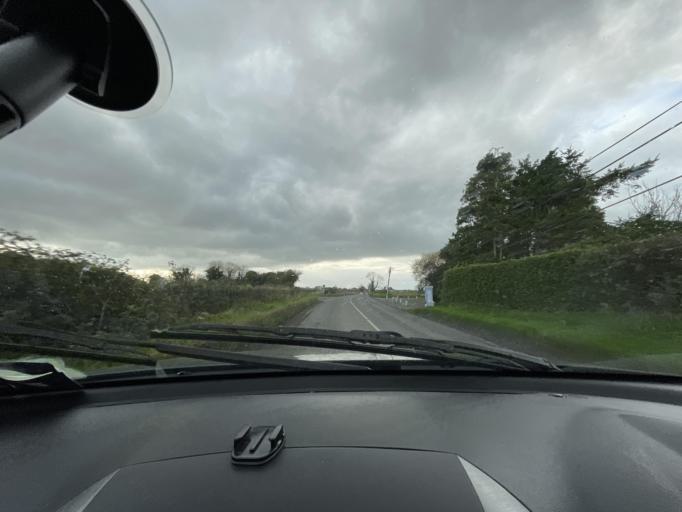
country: IE
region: Leinster
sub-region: Lu
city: Termonfeckin
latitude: 53.7516
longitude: -6.2837
